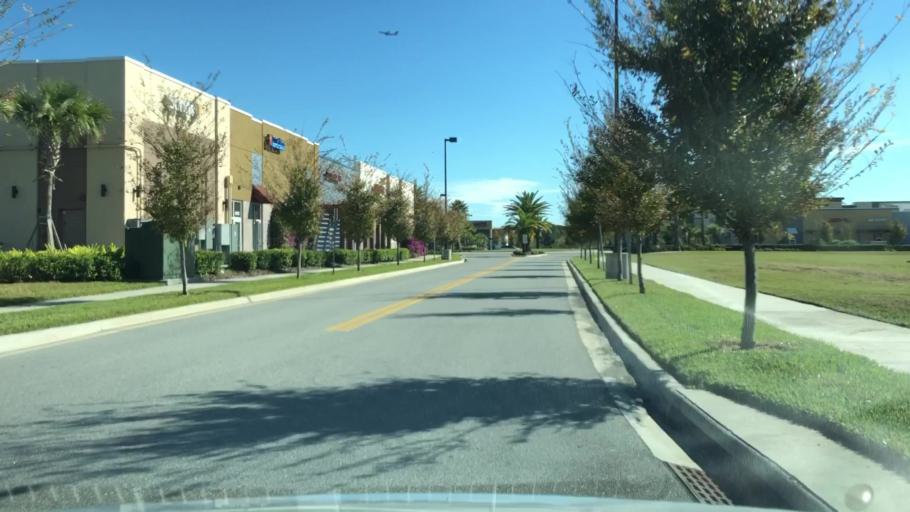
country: US
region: Florida
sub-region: Orange County
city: Conway
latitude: 28.4659
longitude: -81.3076
